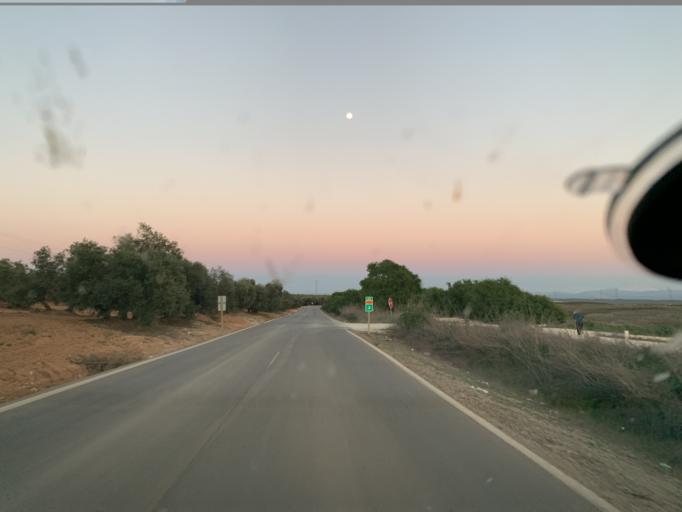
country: ES
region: Andalusia
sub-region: Provincia de Sevilla
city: Pedrera
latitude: 37.2150
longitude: -4.8508
